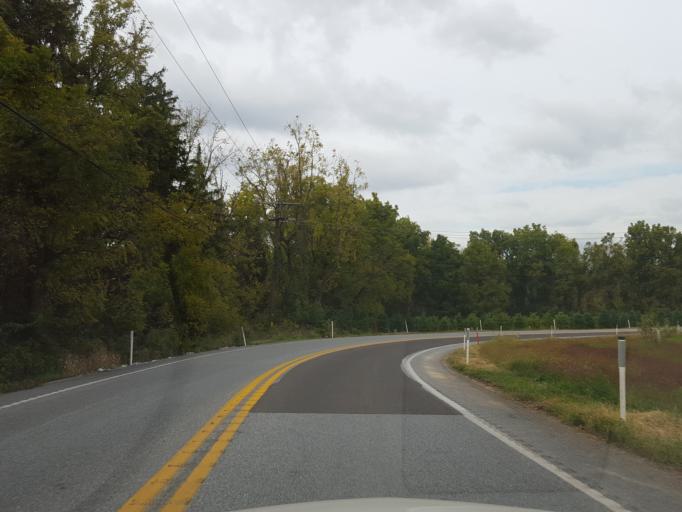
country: US
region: Pennsylvania
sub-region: York County
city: Yoe
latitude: 39.9334
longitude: -76.6554
